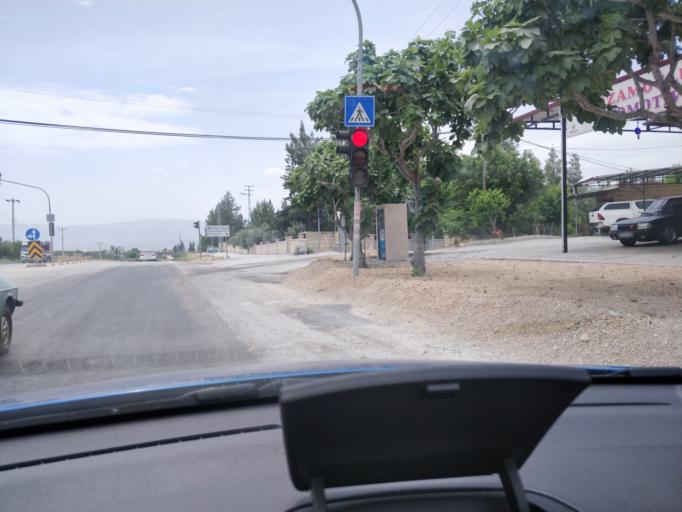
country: TR
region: Mersin
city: Mut
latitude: 36.6168
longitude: 33.4413
